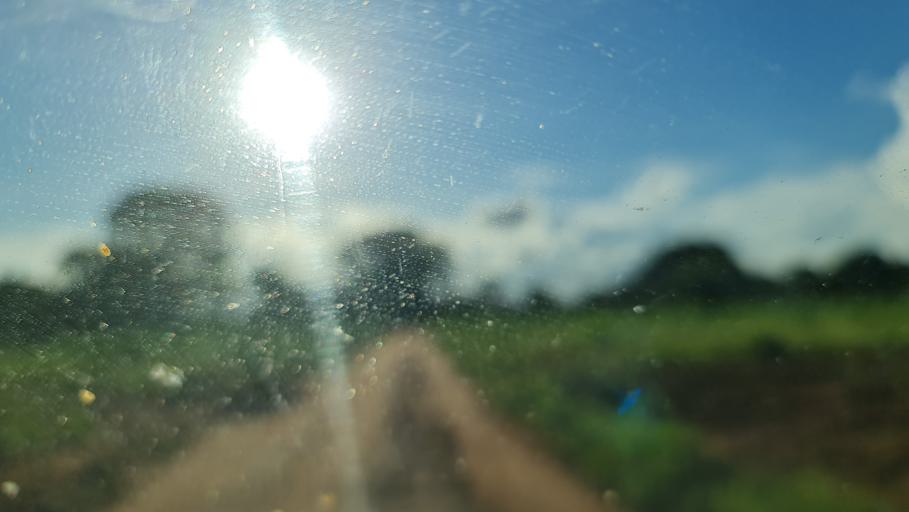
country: MZ
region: Nampula
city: Ilha de Mocambique
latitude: -14.9438
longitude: 40.1587
